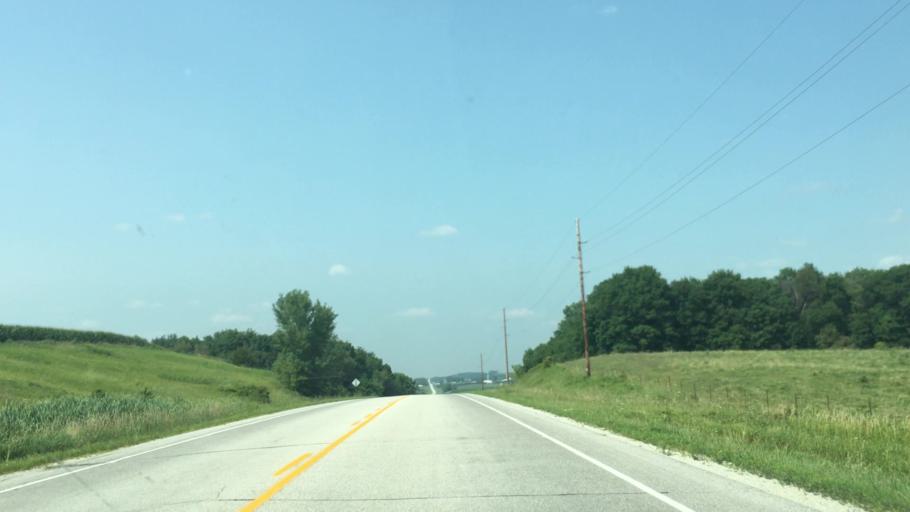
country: US
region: Minnesota
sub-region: Fillmore County
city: Harmony
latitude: 43.5851
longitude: -91.9298
